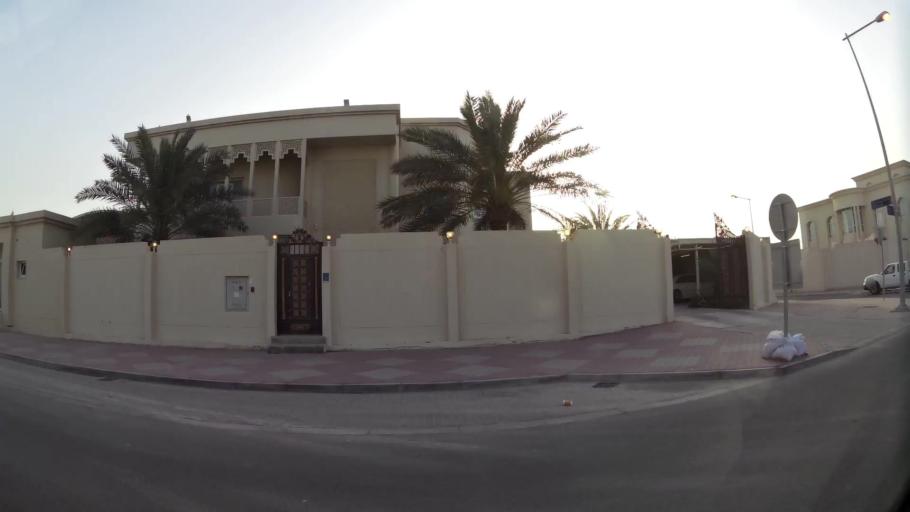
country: QA
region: Baladiyat ar Rayyan
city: Ar Rayyan
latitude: 25.2381
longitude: 51.4461
